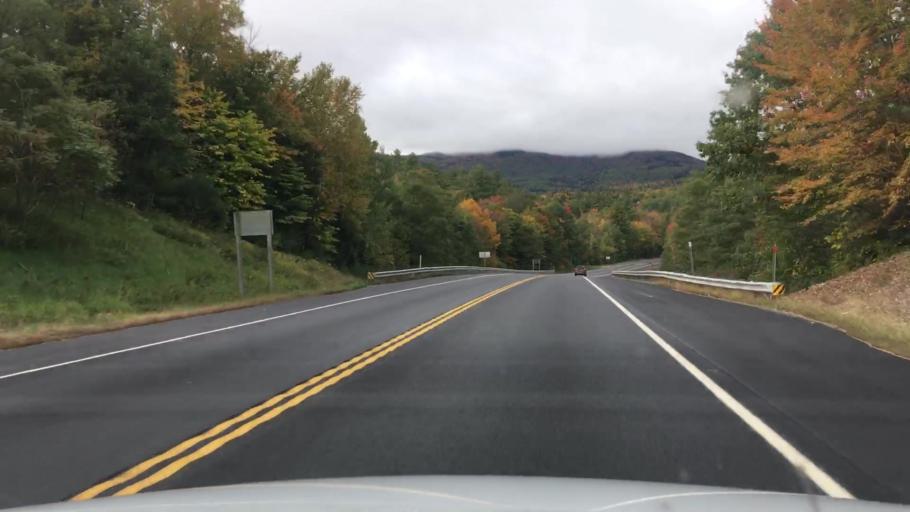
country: US
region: New Hampshire
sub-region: Coos County
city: Gorham
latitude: 44.3872
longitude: -71.0110
